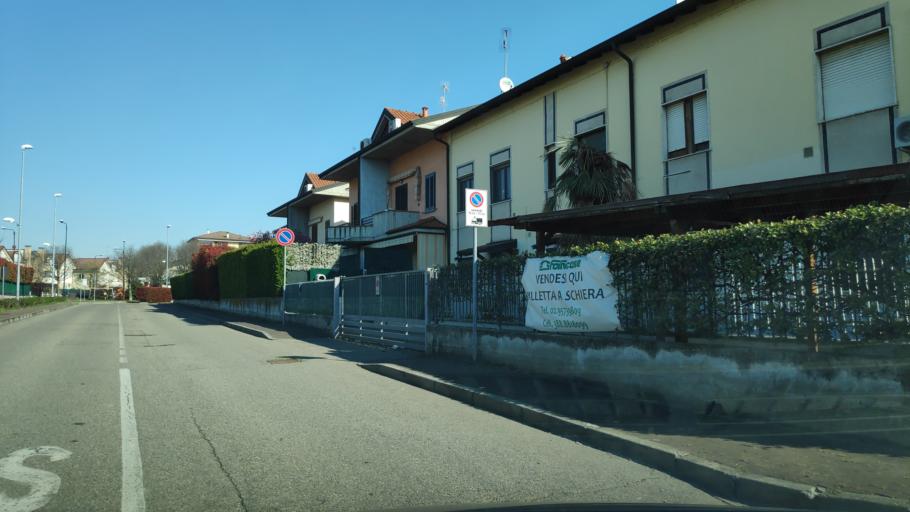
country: IT
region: Lombardy
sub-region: Citta metropolitana di Milano
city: Liscate
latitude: 45.4806
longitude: 9.4050
